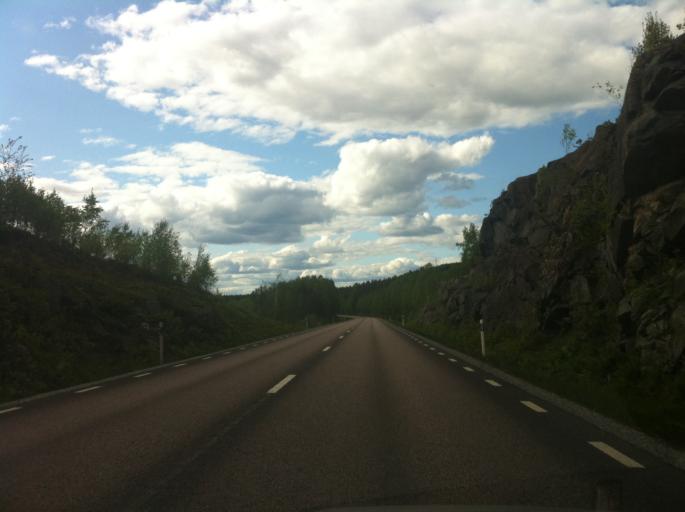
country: SE
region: Vaermland
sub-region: Storfors Kommun
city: Storfors
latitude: 59.6388
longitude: 14.2565
